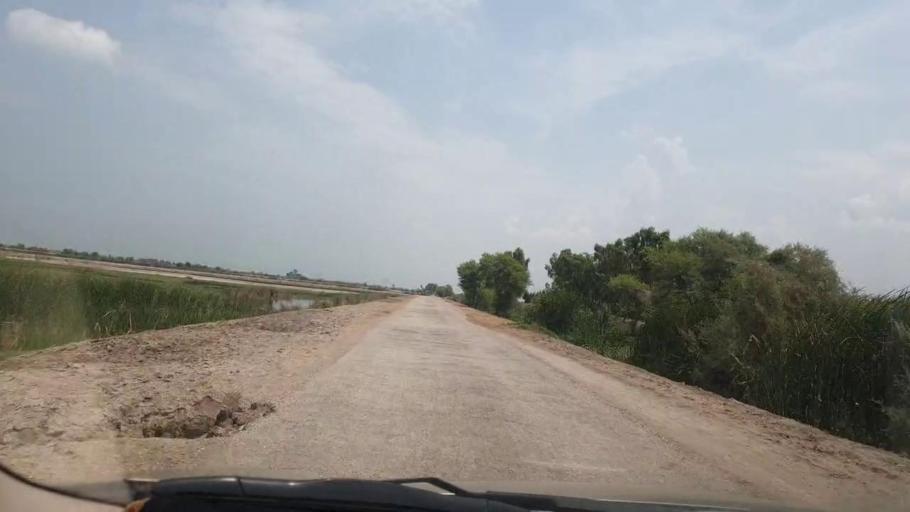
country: PK
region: Sindh
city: Larkana
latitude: 27.6074
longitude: 68.1679
